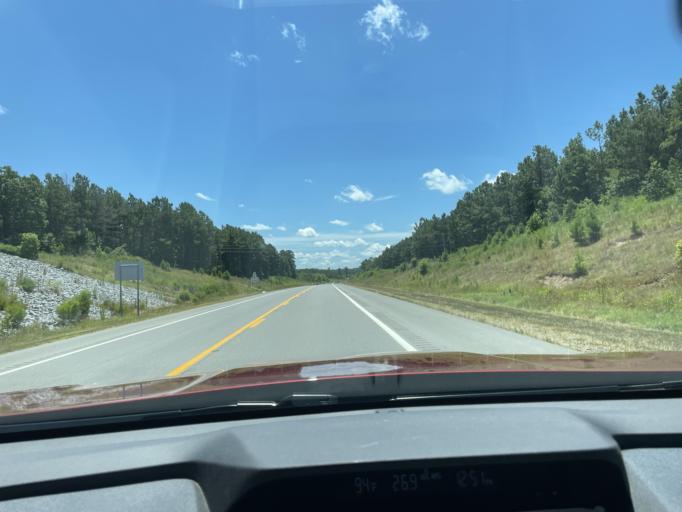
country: US
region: Arkansas
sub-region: Lincoln County
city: Star City
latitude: 33.9307
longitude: -91.8887
